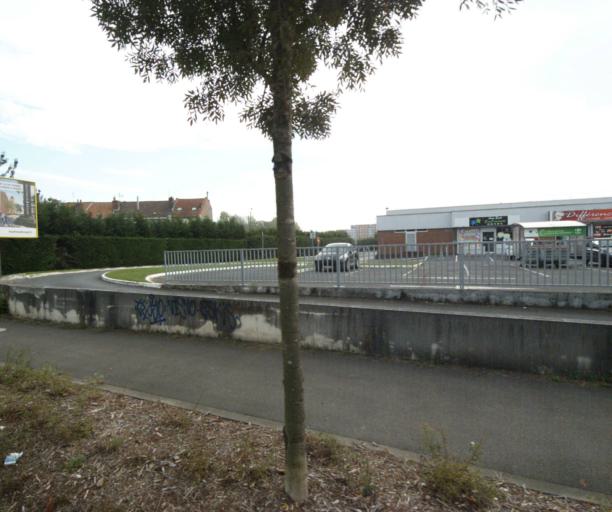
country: FR
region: Nord-Pas-de-Calais
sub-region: Departement du Nord
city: Seclin
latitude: 50.5422
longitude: 3.0211
